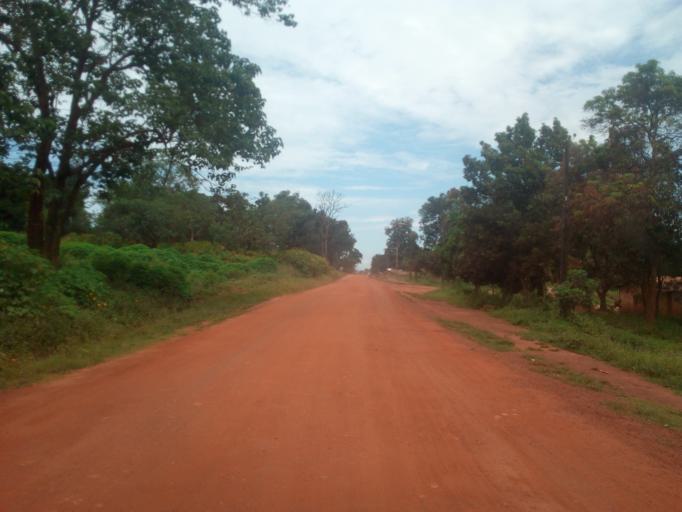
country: CF
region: Ouaka
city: Bambari
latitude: 5.7704
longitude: 20.6724
